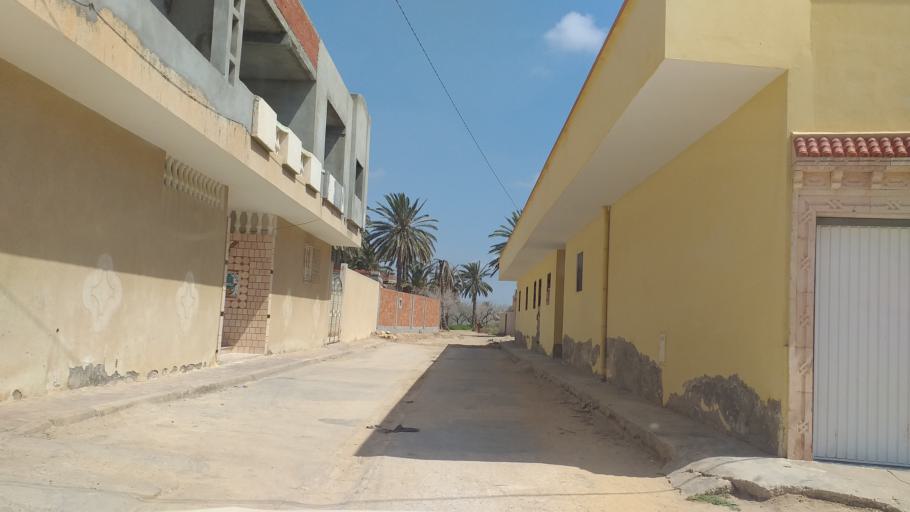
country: TN
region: Qabis
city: Gabes
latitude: 33.9445
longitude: 10.0638
